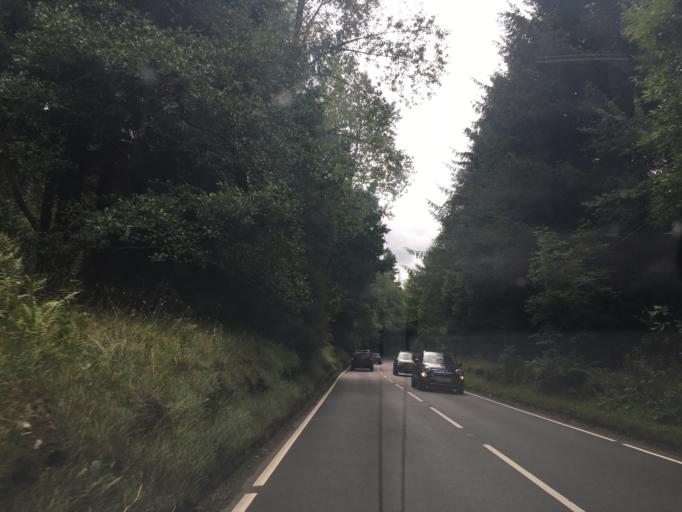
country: GB
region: Scotland
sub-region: Stirling
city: Callander
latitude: 56.3214
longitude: -4.3283
